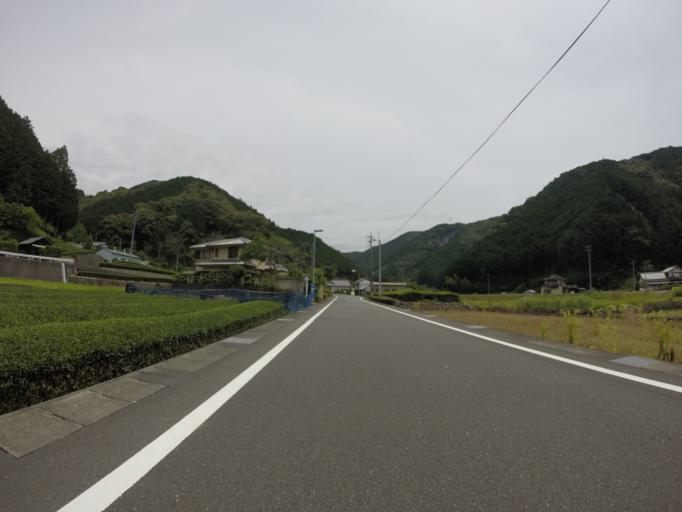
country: JP
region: Shizuoka
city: Shizuoka-shi
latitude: 35.0177
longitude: 138.2819
